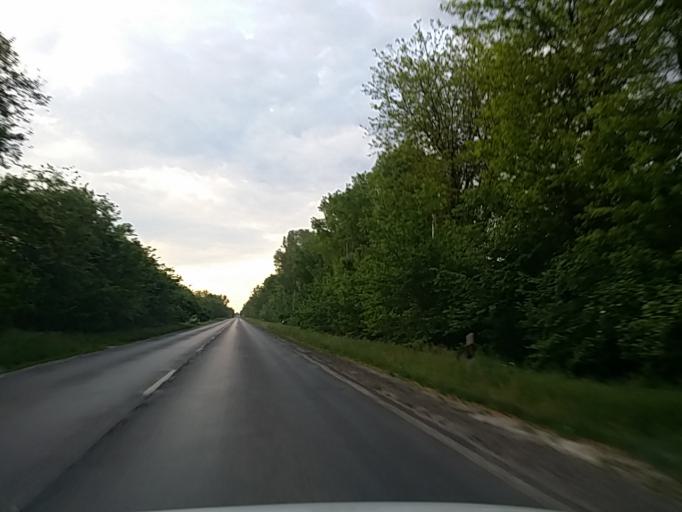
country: HU
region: Bacs-Kiskun
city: Lajosmizse
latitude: 47.0151
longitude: 19.5745
